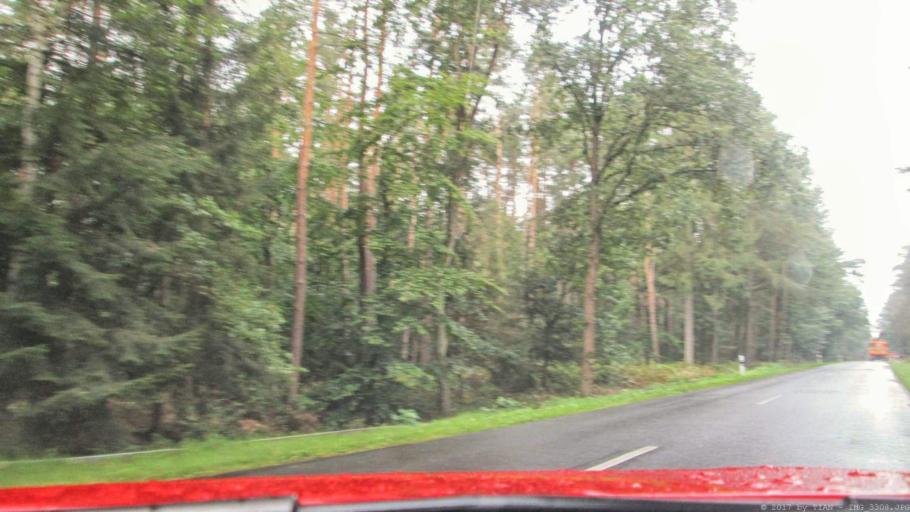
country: DE
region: Lower Saxony
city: Schoneworde
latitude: 52.5970
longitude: 10.6406
